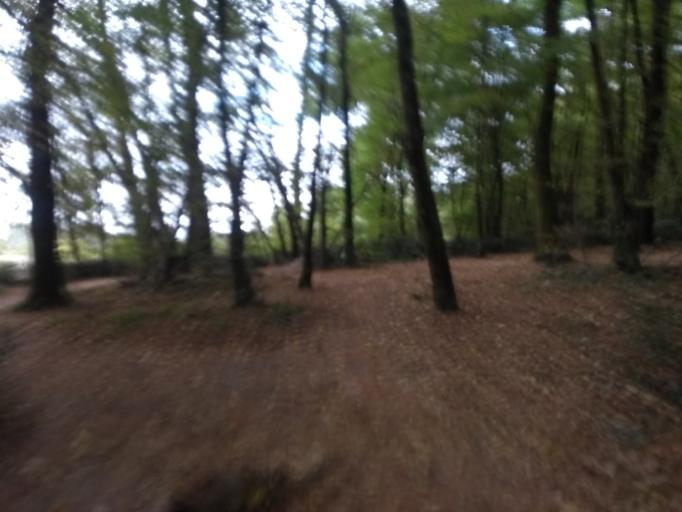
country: FR
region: Aquitaine
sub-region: Departement de la Gironde
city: Pessac
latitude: 44.8200
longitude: -0.6469
